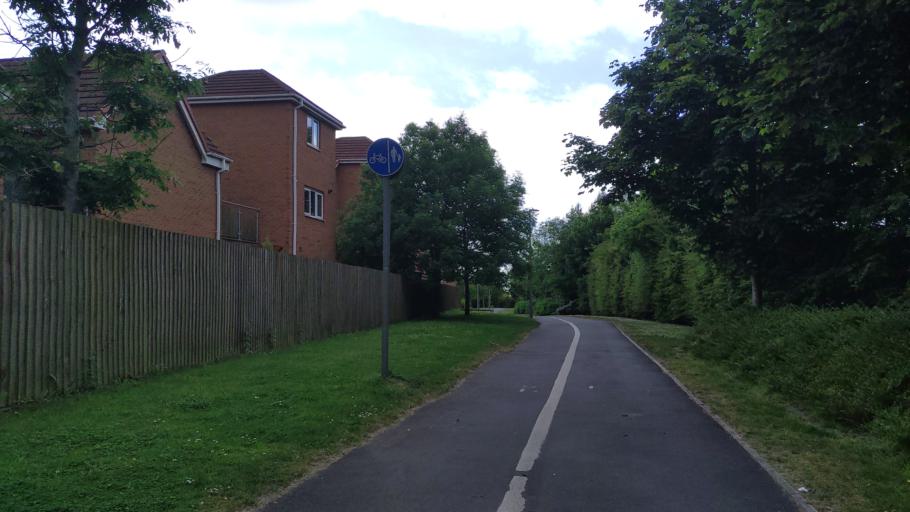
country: GB
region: England
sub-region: Lancashire
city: Clayton-le-Woods
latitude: 53.6830
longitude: -2.6695
